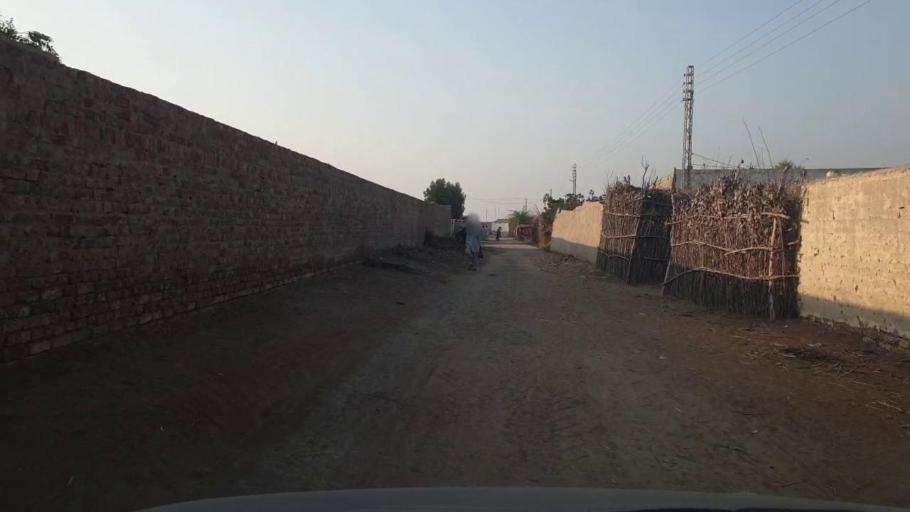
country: PK
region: Sindh
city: Mirwah Gorchani
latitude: 25.3733
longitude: 69.1241
